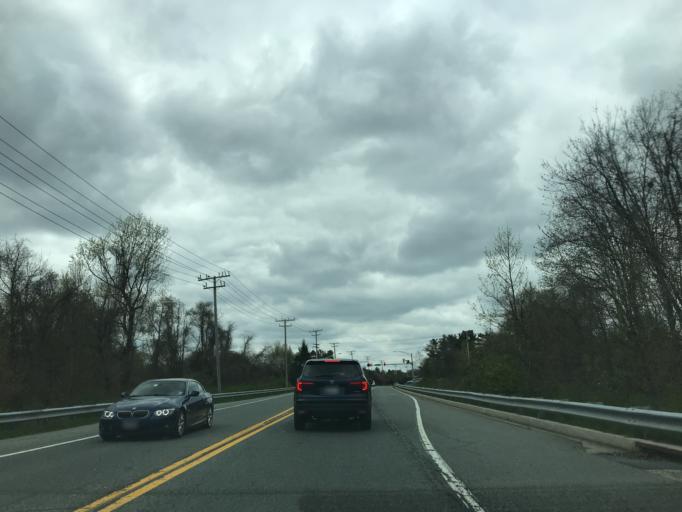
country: US
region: Maryland
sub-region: Harford County
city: Bel Air South
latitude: 39.4919
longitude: -76.3220
